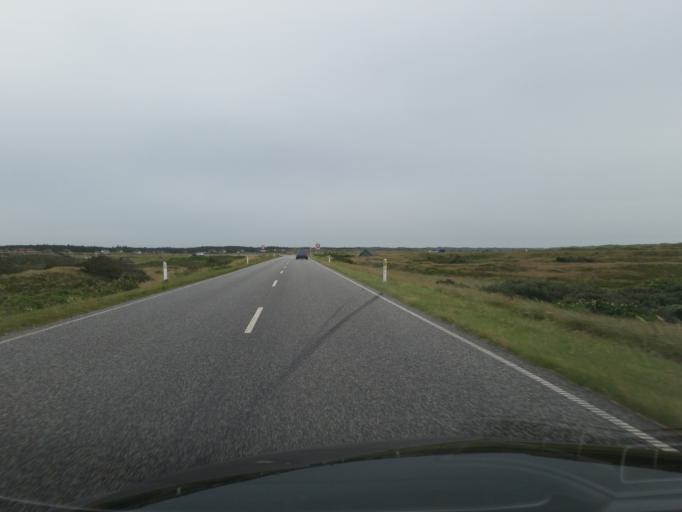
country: DK
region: Central Jutland
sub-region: Ringkobing-Skjern Kommune
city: Hvide Sande
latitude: 55.8217
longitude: 8.1809
